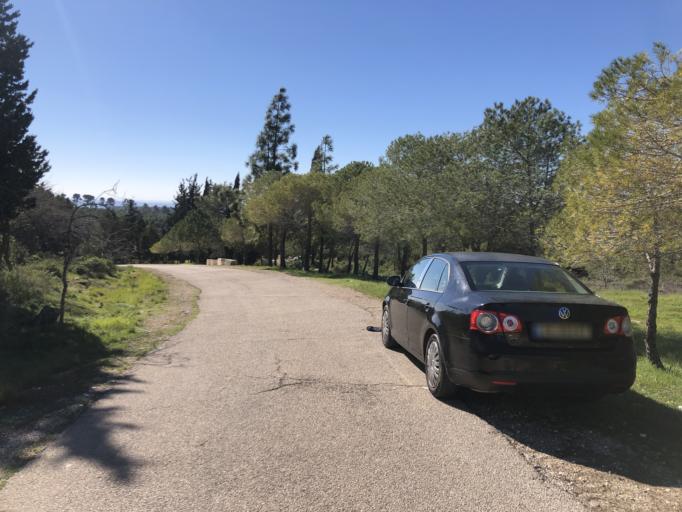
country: IL
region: Jerusalem
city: Zur Hadassa
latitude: 31.7477
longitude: 35.0488
